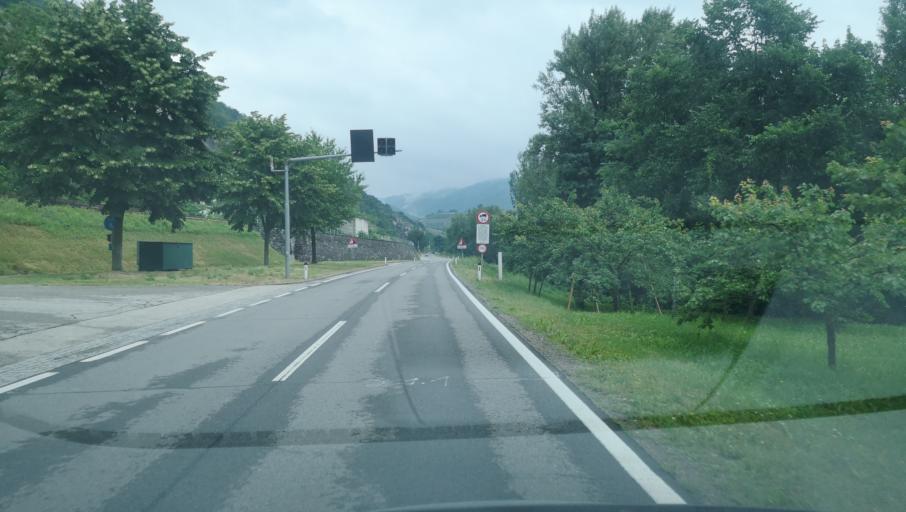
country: AT
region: Lower Austria
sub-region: Politischer Bezirk Krems
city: Spitz
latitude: 48.3479
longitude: 15.4049
